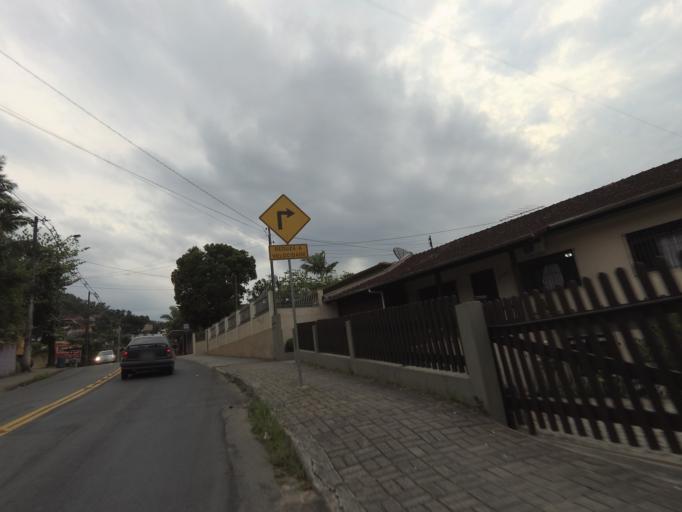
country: BR
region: Santa Catarina
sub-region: Blumenau
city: Blumenau
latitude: -26.8738
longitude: -49.0507
